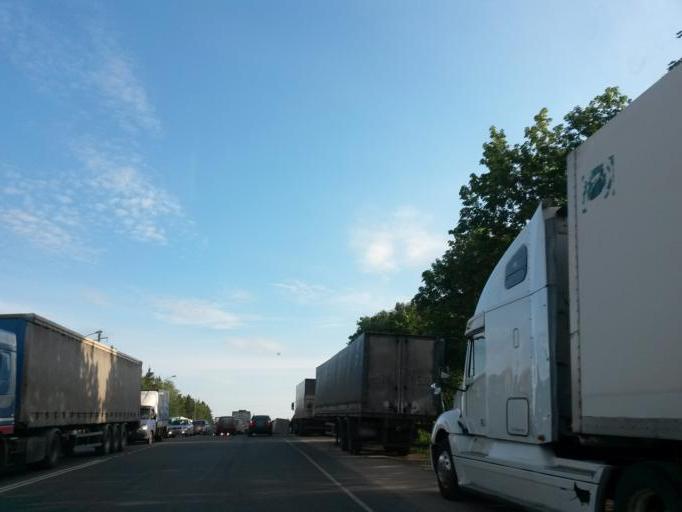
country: RU
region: Moskovskaya
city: Yam
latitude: 55.4768
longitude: 37.7150
